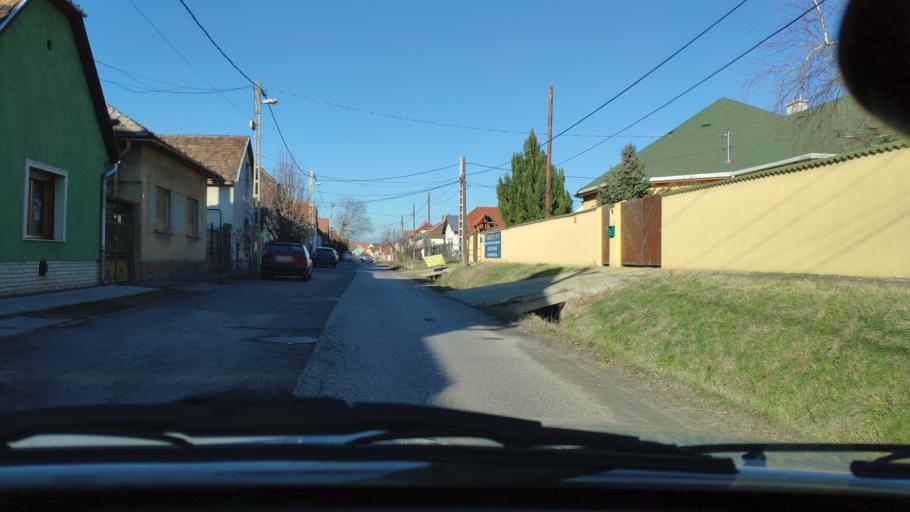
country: HU
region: Budapest
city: Budapest XXIII. keruelet
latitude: 47.4068
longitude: 19.1229
